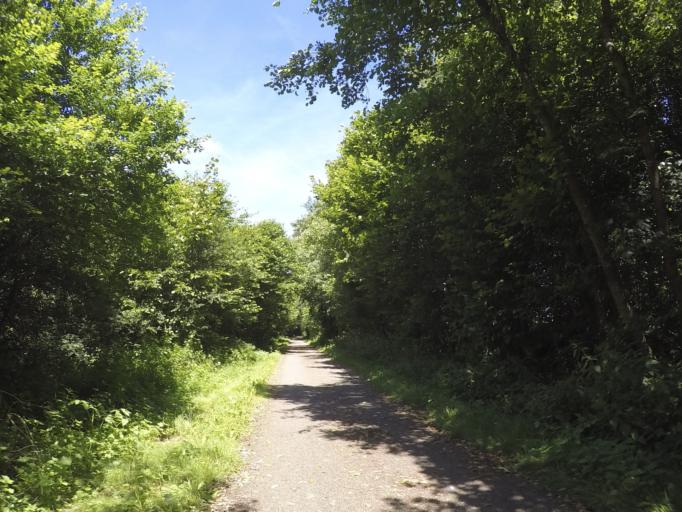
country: BE
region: Wallonia
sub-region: Province de Namur
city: Hamois
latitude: 50.3510
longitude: 5.1749
